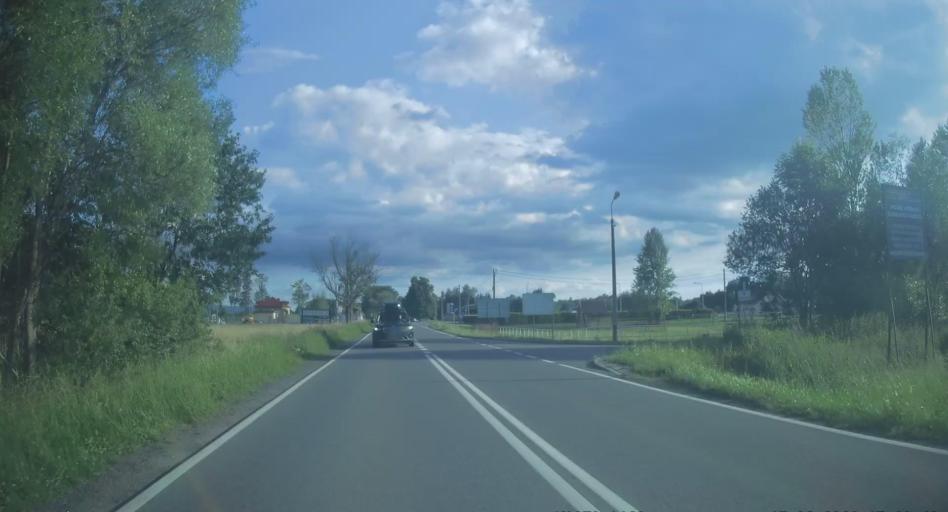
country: PL
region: Lesser Poland Voivodeship
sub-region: Powiat oswiecimski
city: Grojec
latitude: 49.9725
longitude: 19.2208
